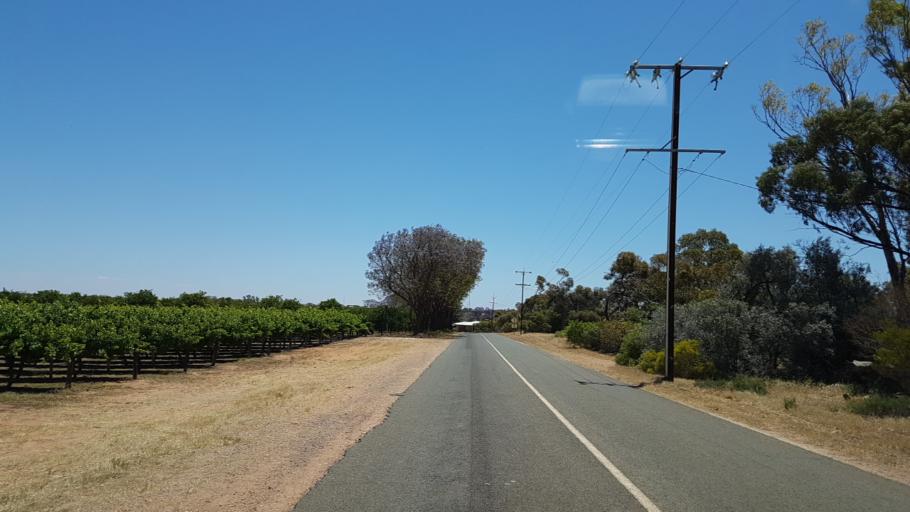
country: AU
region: South Australia
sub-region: Loxton Waikerie
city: Waikerie
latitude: -34.1684
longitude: 140.0370
